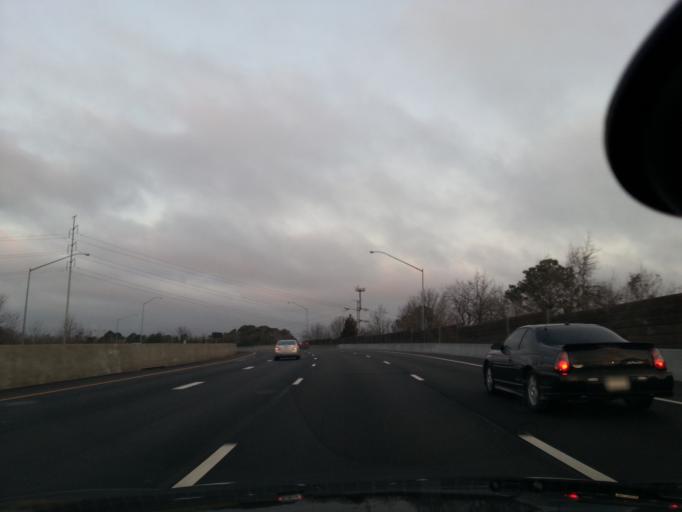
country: US
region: Virginia
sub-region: City of Chesapeake
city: Chesapeake
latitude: 36.8456
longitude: -76.2418
